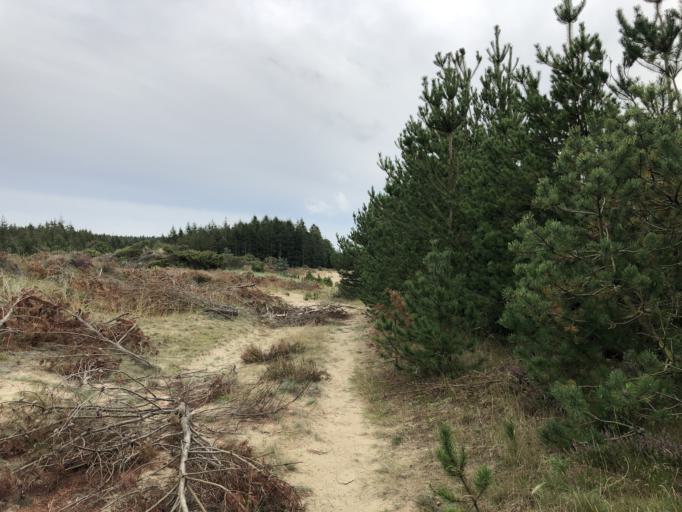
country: DK
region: Central Jutland
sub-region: Holstebro Kommune
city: Ulfborg
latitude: 56.2487
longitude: 8.4325
